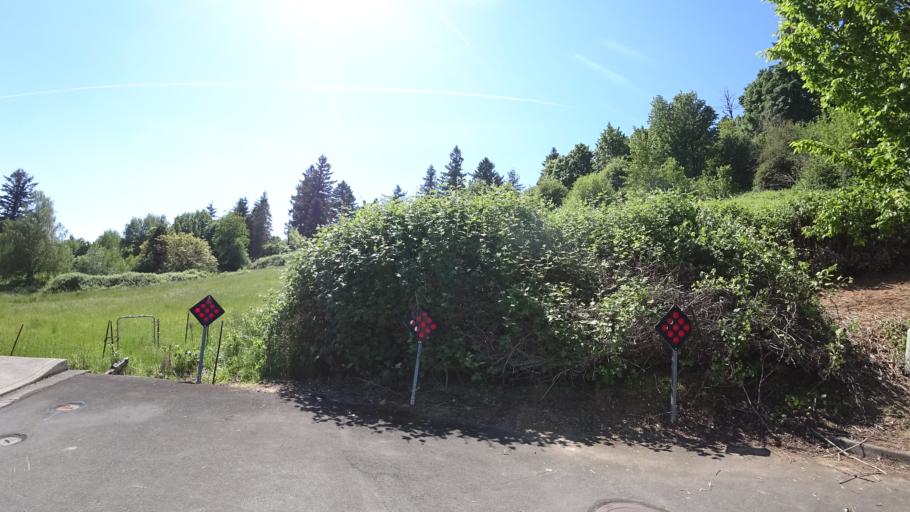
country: US
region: Oregon
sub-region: Multnomah County
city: Gresham
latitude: 45.4791
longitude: -122.4794
